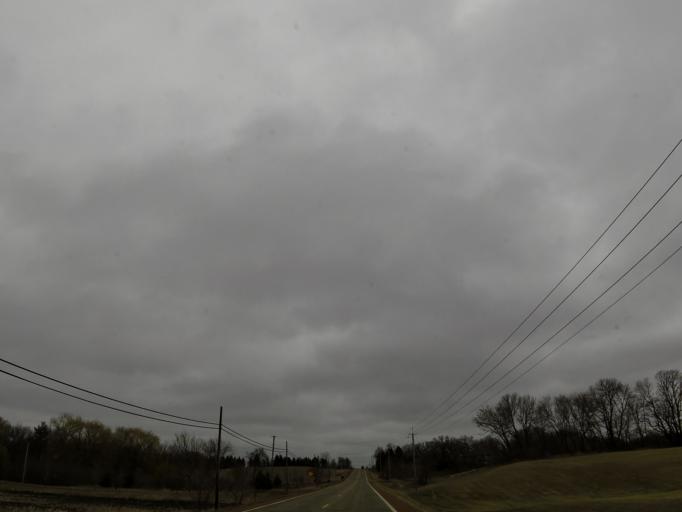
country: US
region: Minnesota
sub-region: Scott County
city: Shakopee
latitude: 44.7595
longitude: -93.5410
